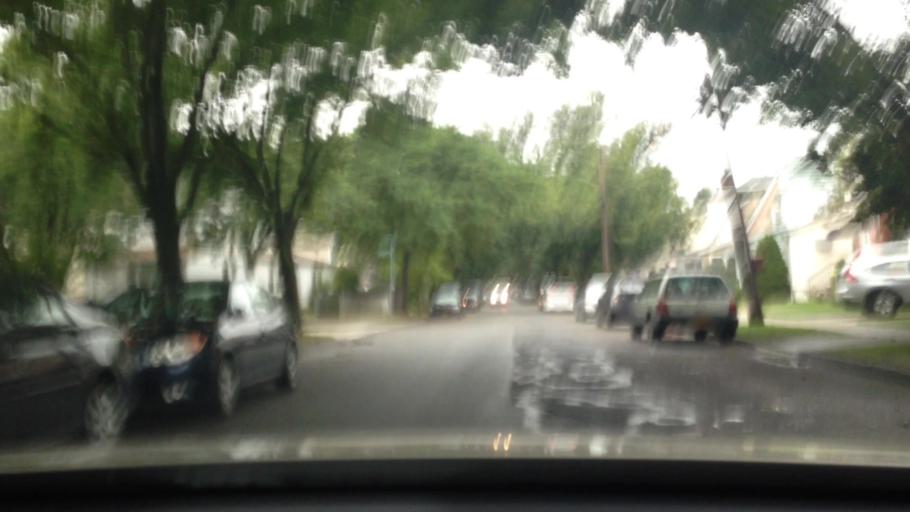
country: US
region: New York
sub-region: Nassau County
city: Bellerose Terrace
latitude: 40.7303
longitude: -73.7293
